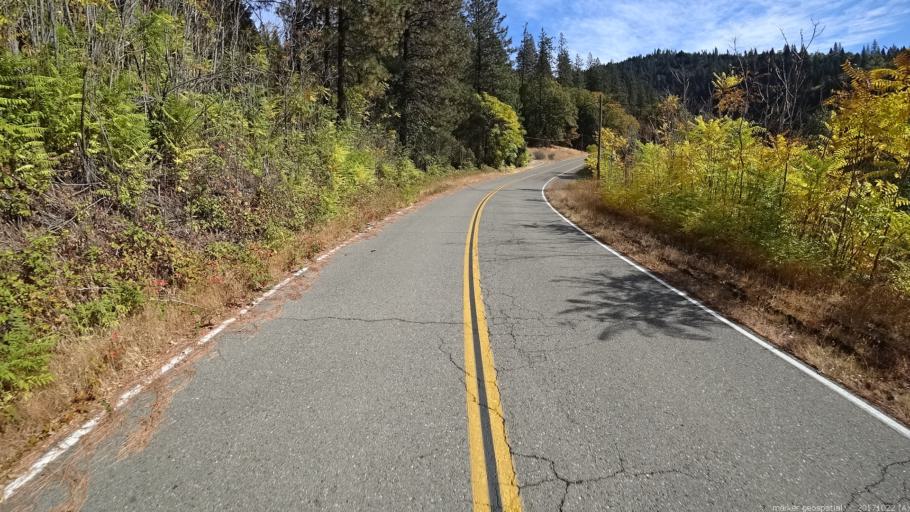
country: US
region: California
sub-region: Siskiyou County
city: Dunsmuir
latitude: 41.0163
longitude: -122.4107
